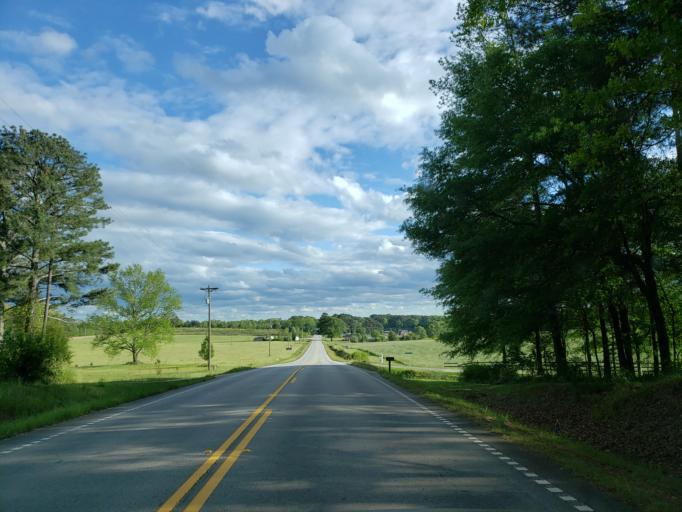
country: US
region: Georgia
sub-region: Haralson County
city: Tallapoosa
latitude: 33.7928
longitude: -85.2963
